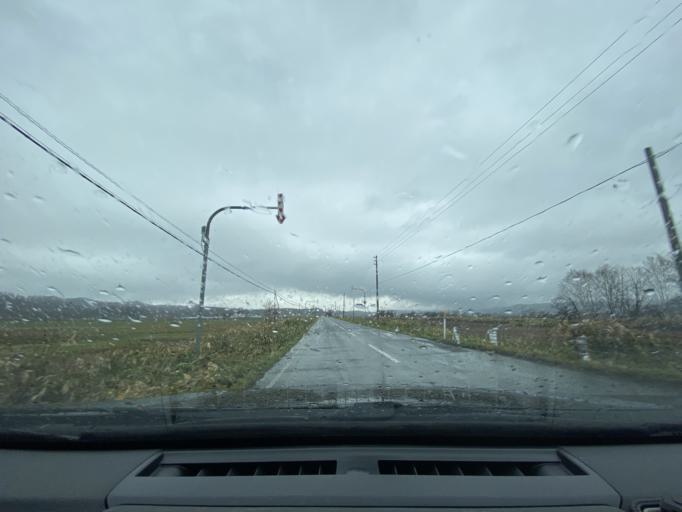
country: JP
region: Hokkaido
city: Fukagawa
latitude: 43.8225
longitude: 141.9023
